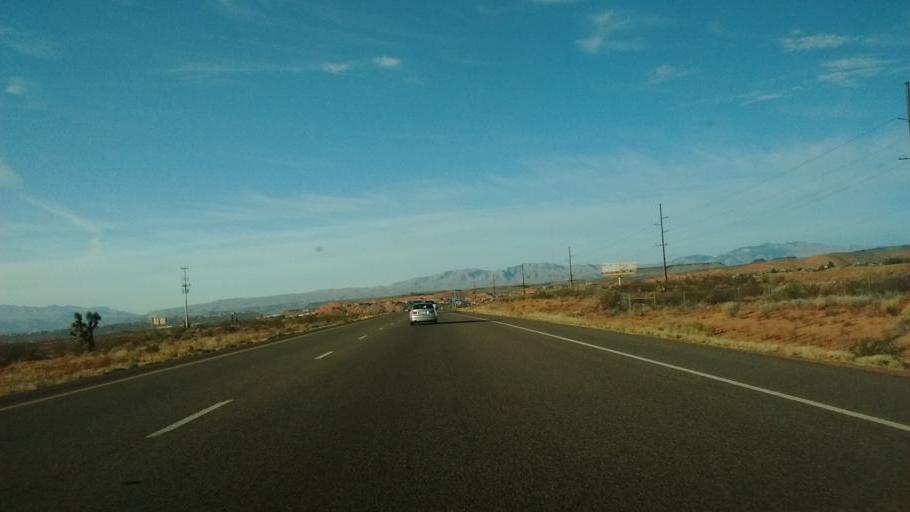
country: US
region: Utah
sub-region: Washington County
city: Washington
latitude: 37.1442
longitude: -113.4968
